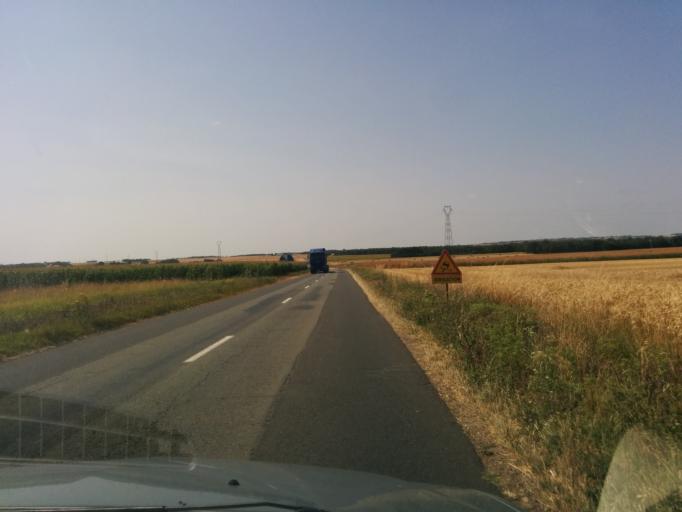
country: FR
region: Poitou-Charentes
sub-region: Departement de la Vienne
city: Neuville-de-Poitou
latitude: 46.7191
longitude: 0.2073
